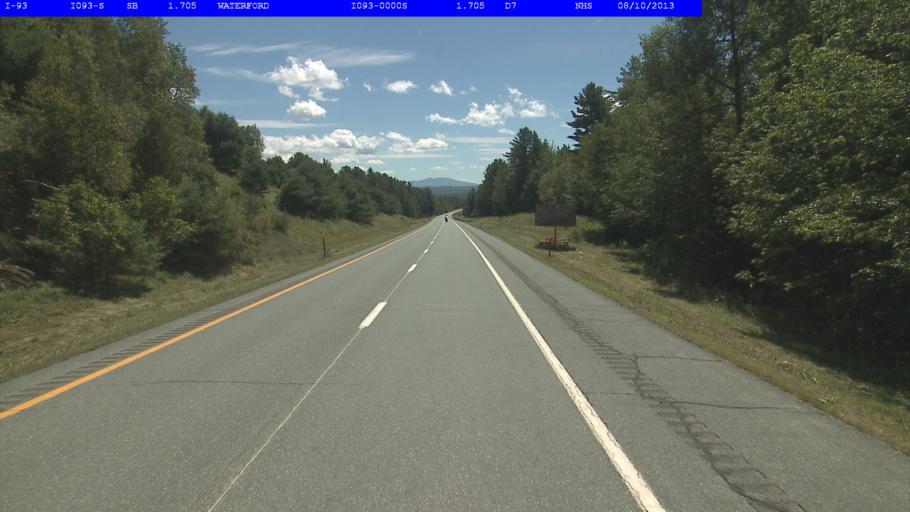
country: US
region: Vermont
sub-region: Caledonia County
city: Saint Johnsbury
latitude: 44.3663
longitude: -71.9033
